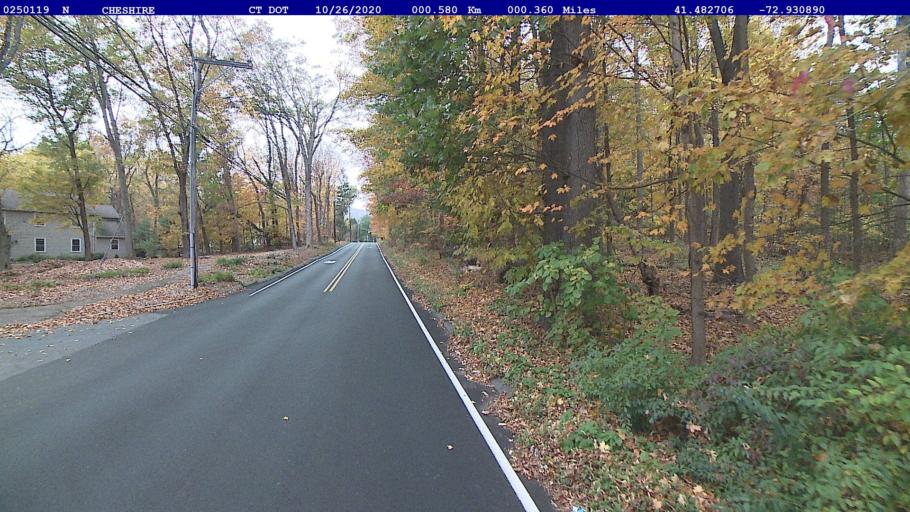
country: US
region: Connecticut
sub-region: New Haven County
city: Cheshire
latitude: 41.4827
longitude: -72.9309
